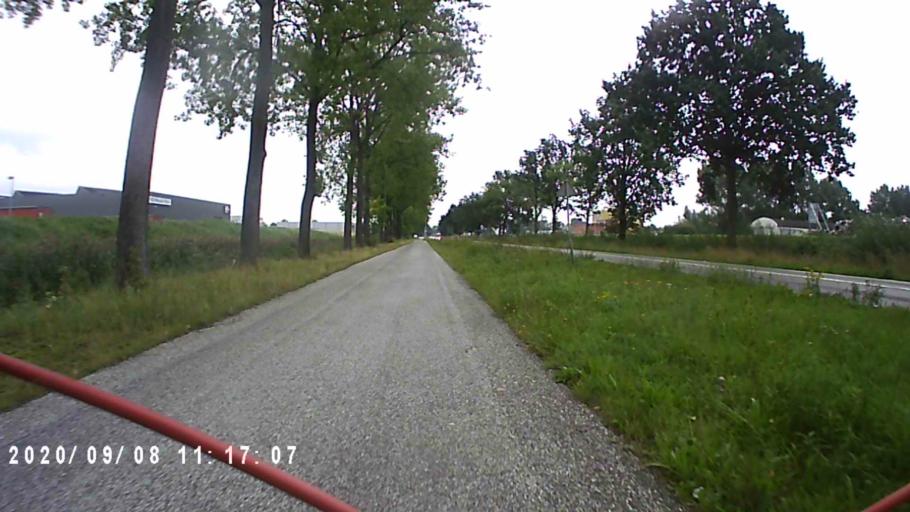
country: NL
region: Groningen
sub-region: Gemeente Hoogezand-Sappemeer
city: Hoogezand
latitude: 53.1707
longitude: 6.7345
